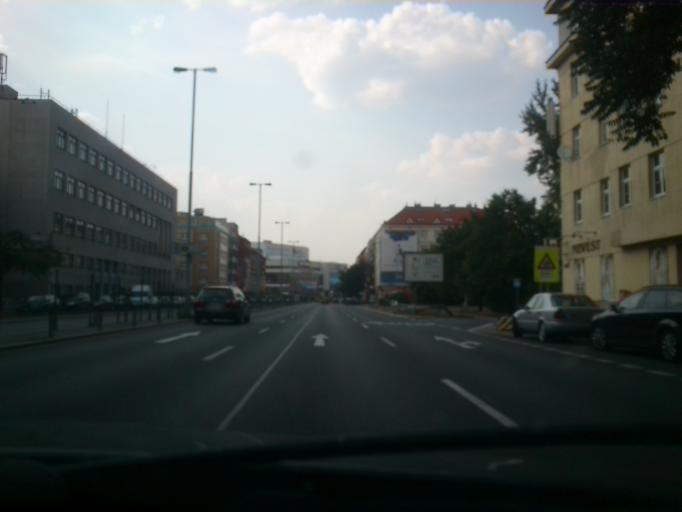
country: CZ
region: Praha
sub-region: Praha 2
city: Vysehrad
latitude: 50.0592
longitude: 14.4340
